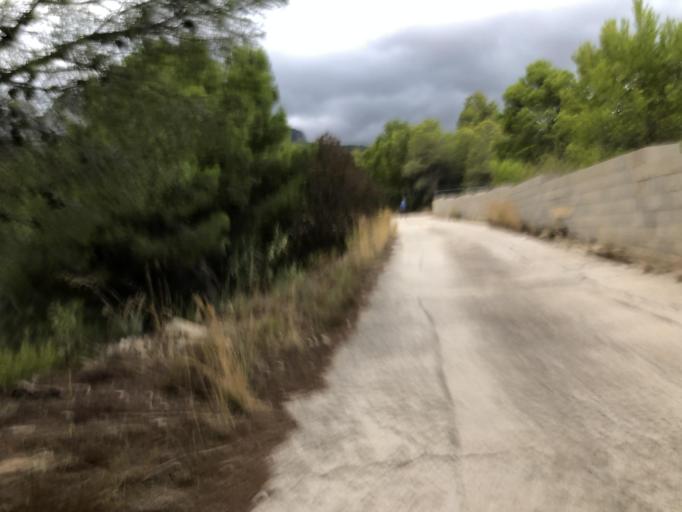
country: ES
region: Valencia
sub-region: Provincia de Alicante
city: Polop
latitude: 38.6367
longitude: -0.1538
